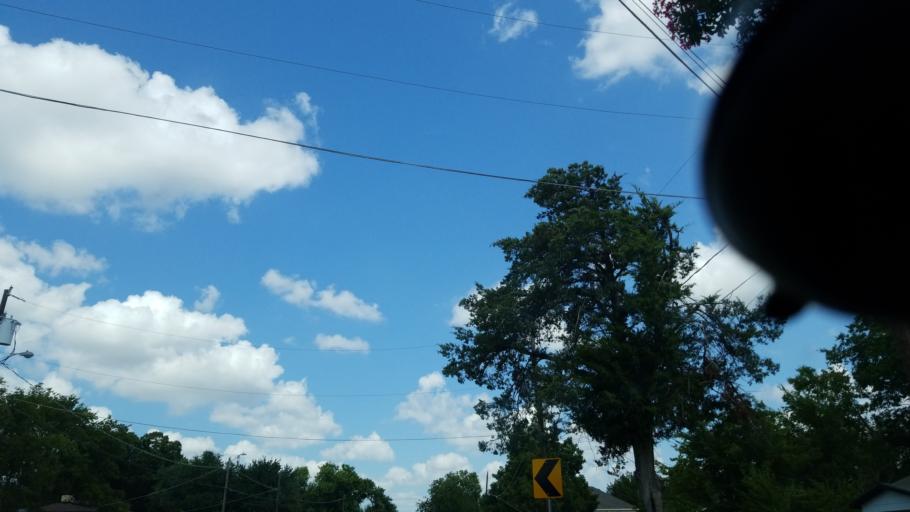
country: US
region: Texas
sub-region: Dallas County
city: Grand Prairie
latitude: 32.7118
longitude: -96.9859
